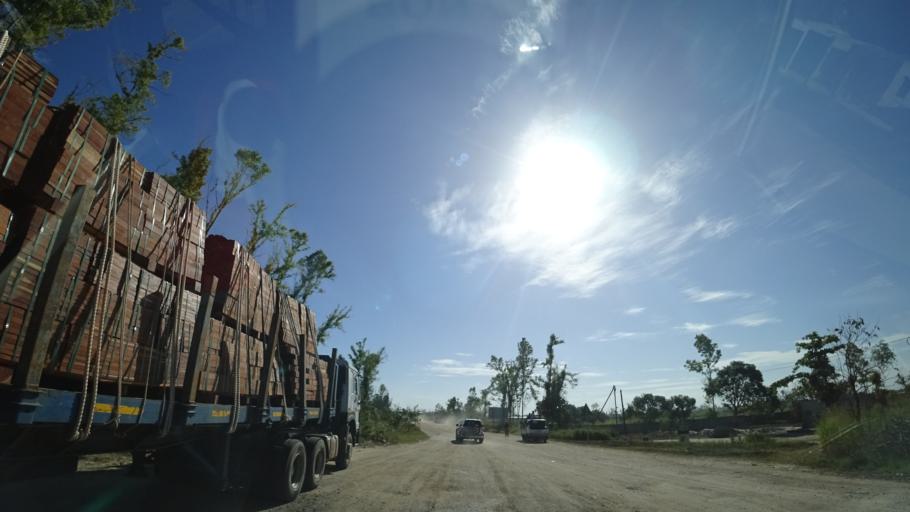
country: MZ
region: Sofala
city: Dondo
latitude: -19.5760
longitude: 34.7230
